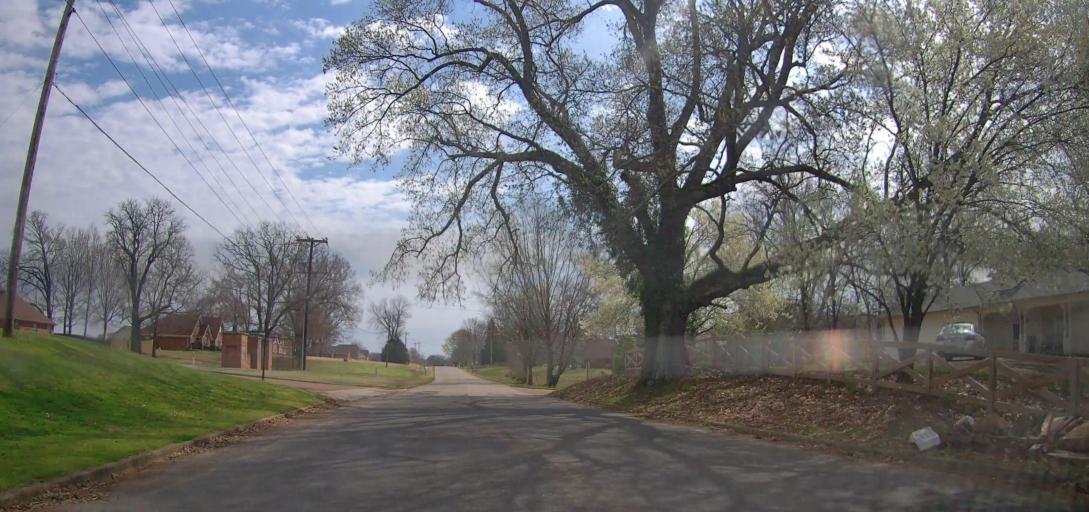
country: US
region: Mississippi
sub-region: De Soto County
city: Olive Branch
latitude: 34.9914
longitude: -89.8581
